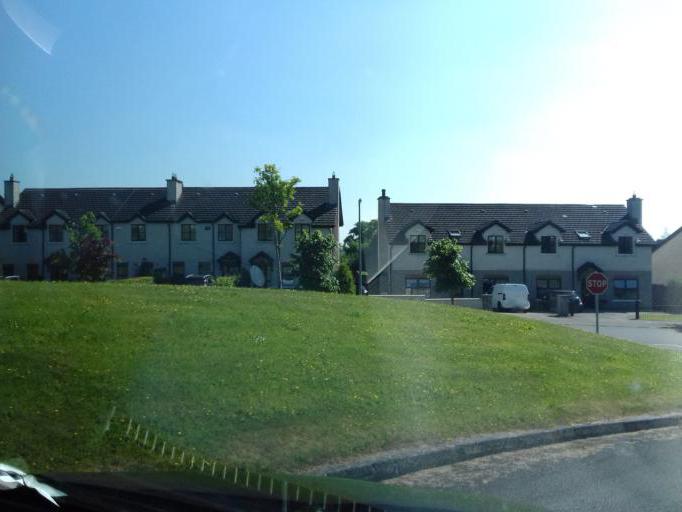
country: IE
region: Leinster
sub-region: An Mhi
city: Slane
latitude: 53.7126
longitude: -6.5532
